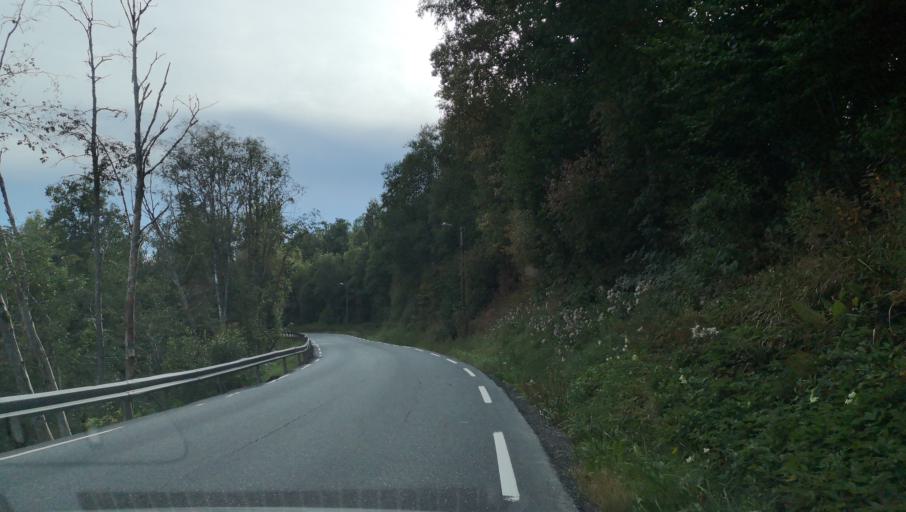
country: NO
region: Ostfold
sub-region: Hobol
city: Tomter
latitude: 59.6818
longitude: 11.0349
